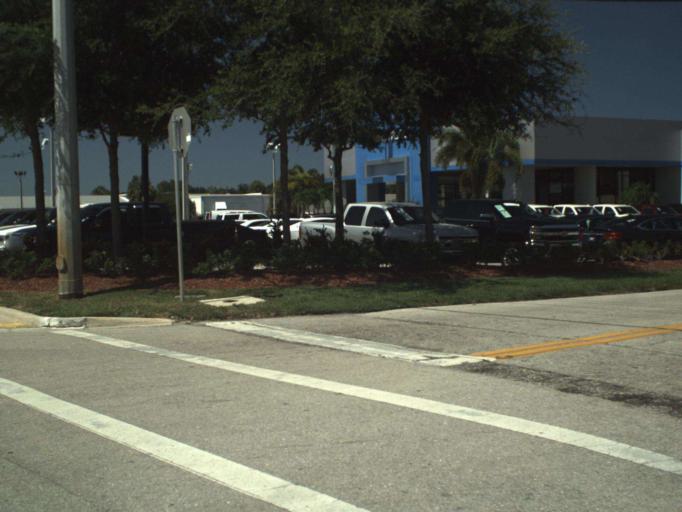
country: US
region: Florida
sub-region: Indian River County
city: Vero Beach
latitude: 27.6197
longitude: -80.3891
